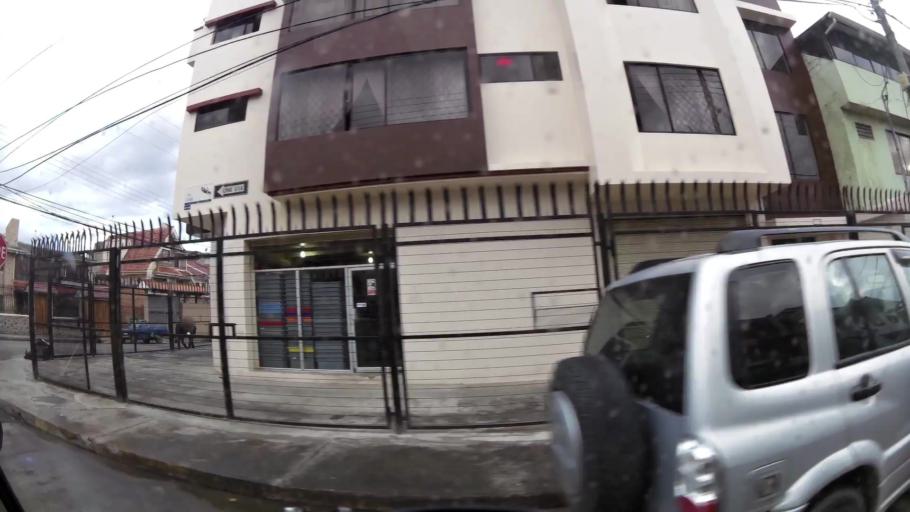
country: EC
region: Azuay
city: Cuenca
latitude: -2.9009
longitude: -79.0241
